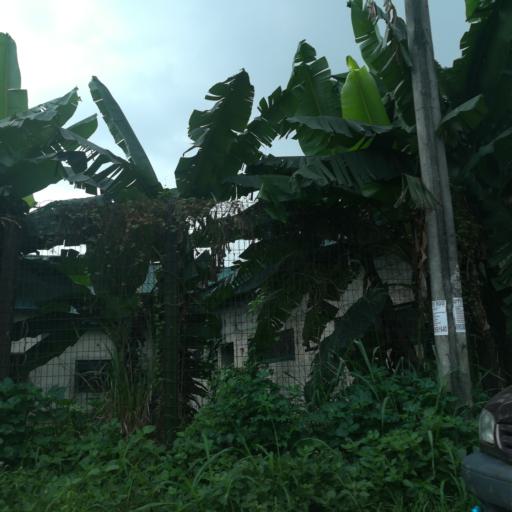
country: NG
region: Rivers
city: Port Harcourt
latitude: 4.8288
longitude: 7.0376
